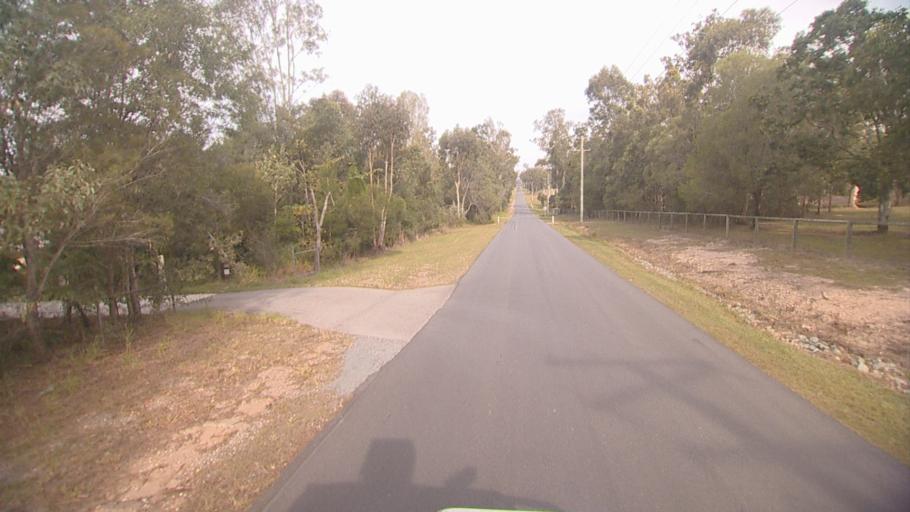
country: AU
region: Queensland
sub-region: Logan
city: Chambers Flat
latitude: -27.7849
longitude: 153.1195
